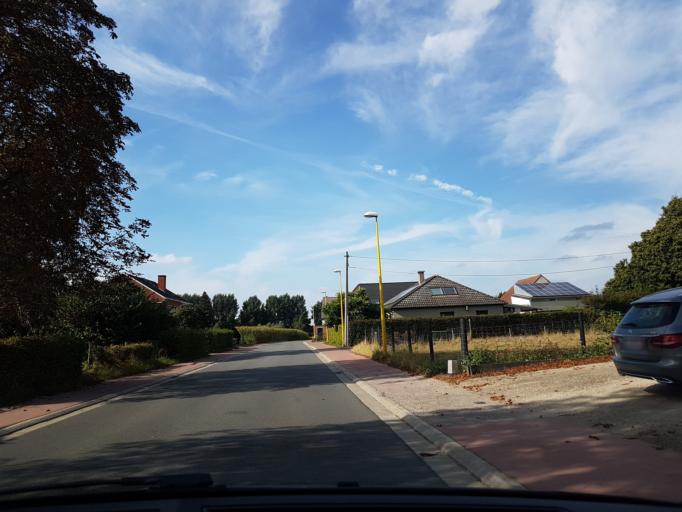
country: BE
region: Flanders
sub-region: Provincie Vlaams-Brabant
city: Grimbergen
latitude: 50.9556
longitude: 4.3931
